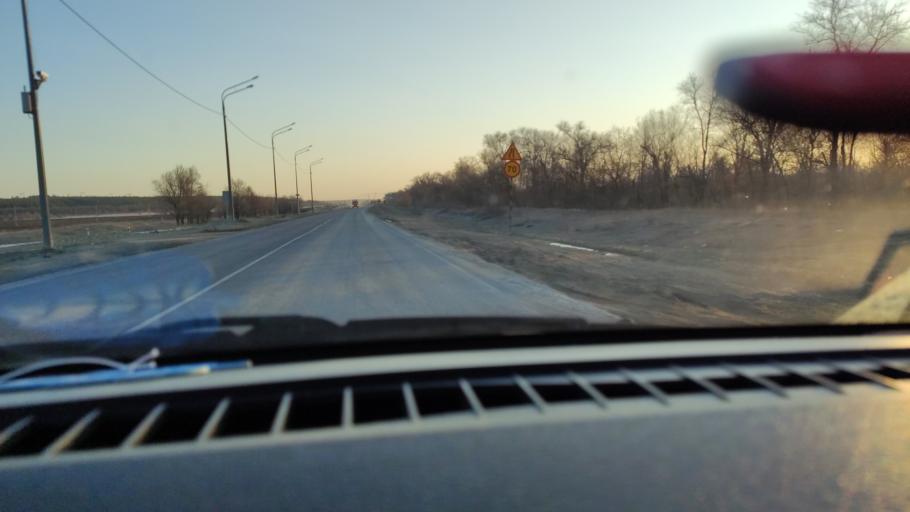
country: RU
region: Saratov
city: Sinodskoye
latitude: 51.9982
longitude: 46.6757
